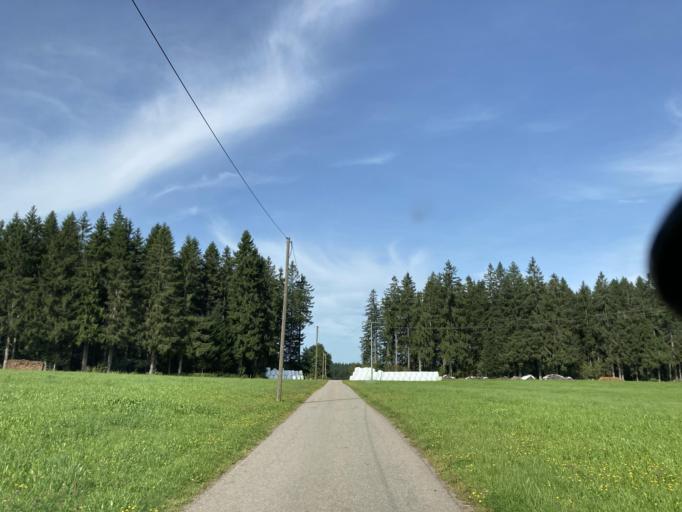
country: DE
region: Baden-Wuerttemberg
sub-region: Freiburg Region
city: Schonwald im Schwarzwald
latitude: 48.0834
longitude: 8.2288
